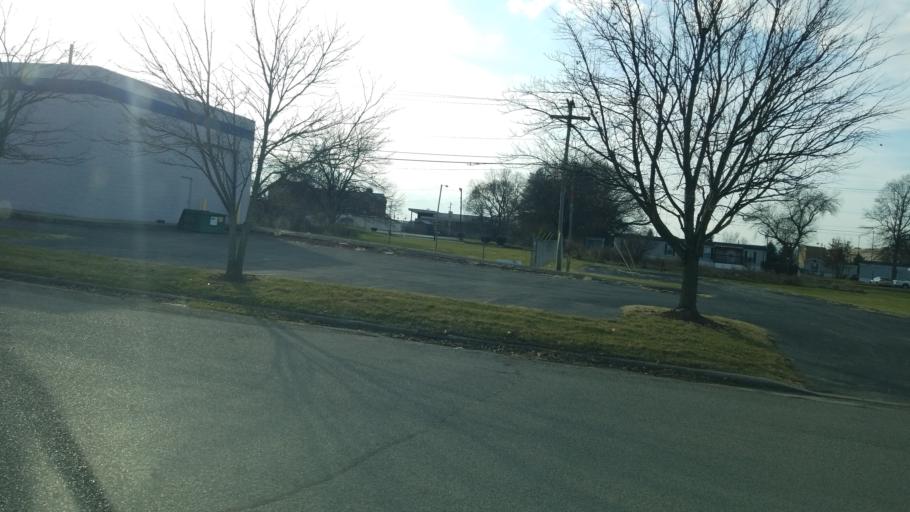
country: US
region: Ohio
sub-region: Ross County
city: Chillicothe
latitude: 39.3644
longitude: -82.9772
